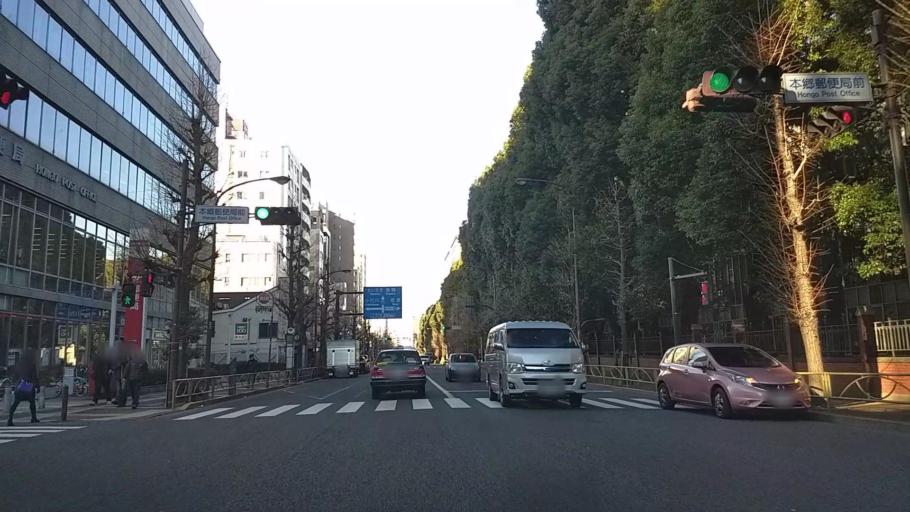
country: JP
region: Tokyo
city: Tokyo
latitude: 35.7120
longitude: 139.7597
